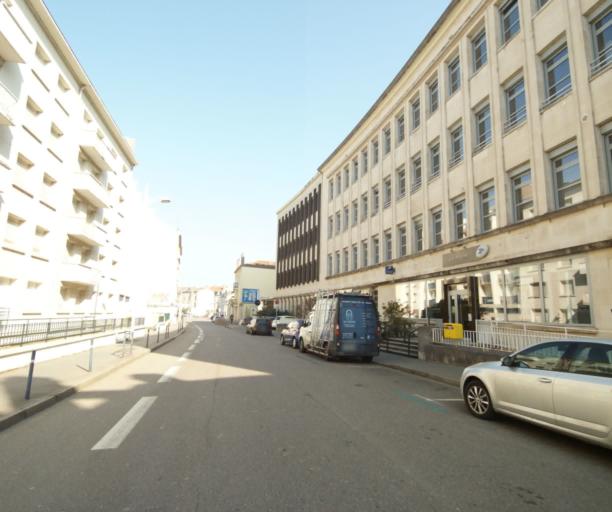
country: FR
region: Lorraine
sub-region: Departement de Meurthe-et-Moselle
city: Nancy
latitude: 48.6880
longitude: 6.1917
